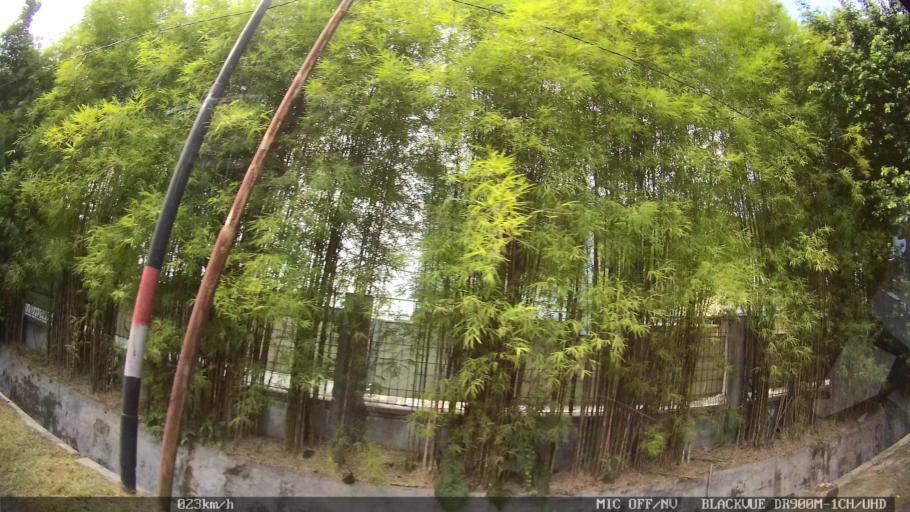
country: ID
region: North Sumatra
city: Medan
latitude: 3.5694
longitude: 98.6795
